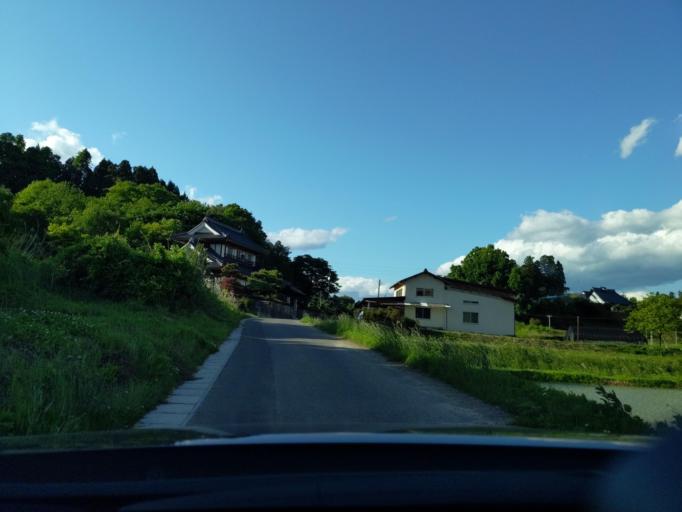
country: JP
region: Fukushima
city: Koriyama
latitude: 37.3918
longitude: 140.4389
